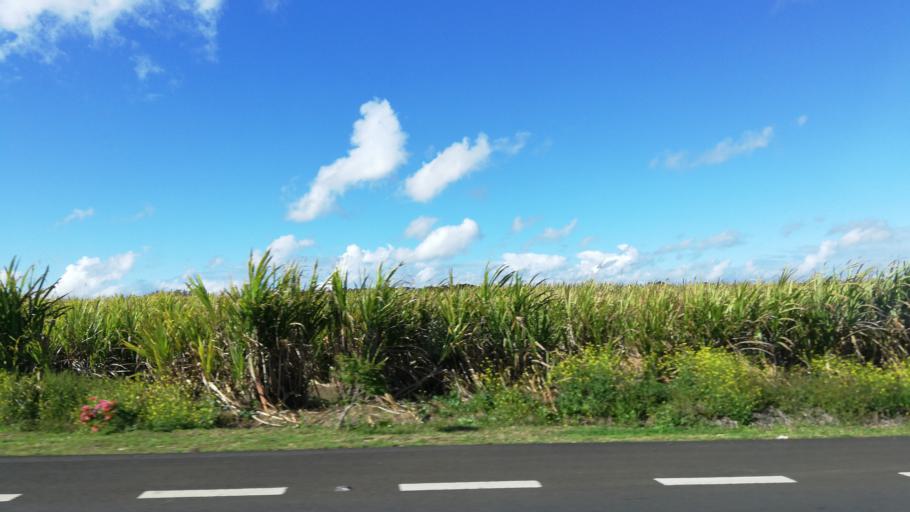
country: MU
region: Moka
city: Saint Pierre
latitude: -20.2322
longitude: 57.5208
